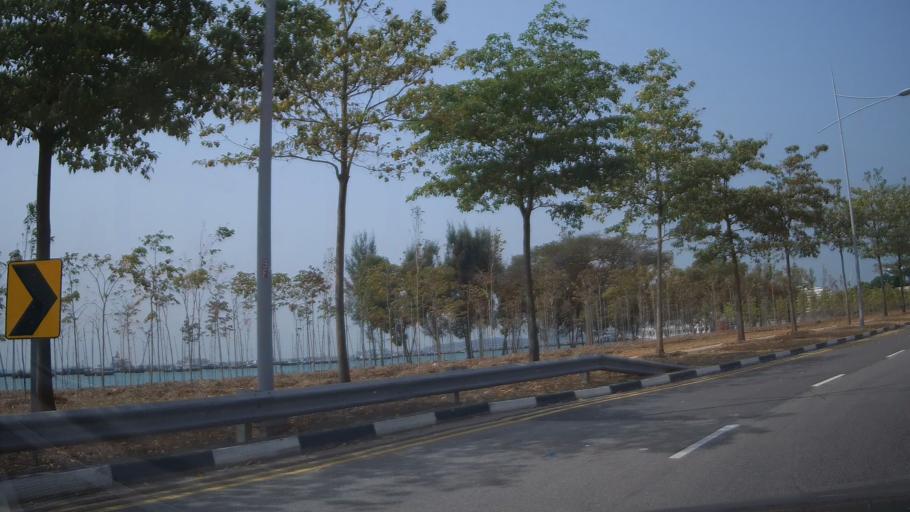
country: SG
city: Singapore
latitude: 1.2702
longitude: 103.8662
